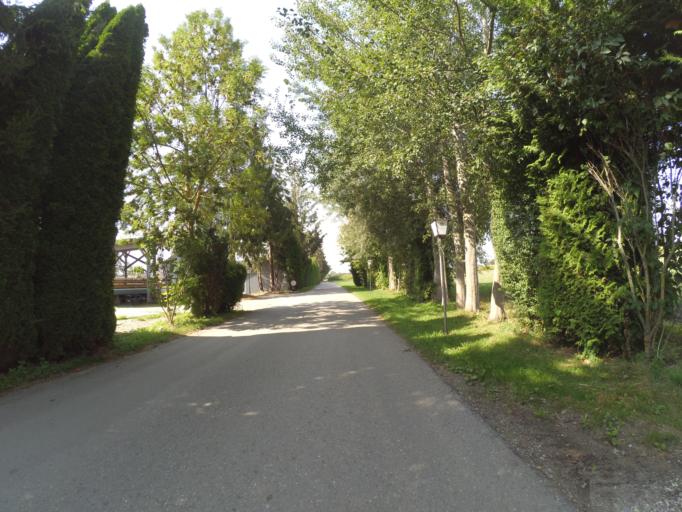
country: DE
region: Bavaria
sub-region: Upper Bavaria
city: Hurlach
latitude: 48.1097
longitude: 10.7751
